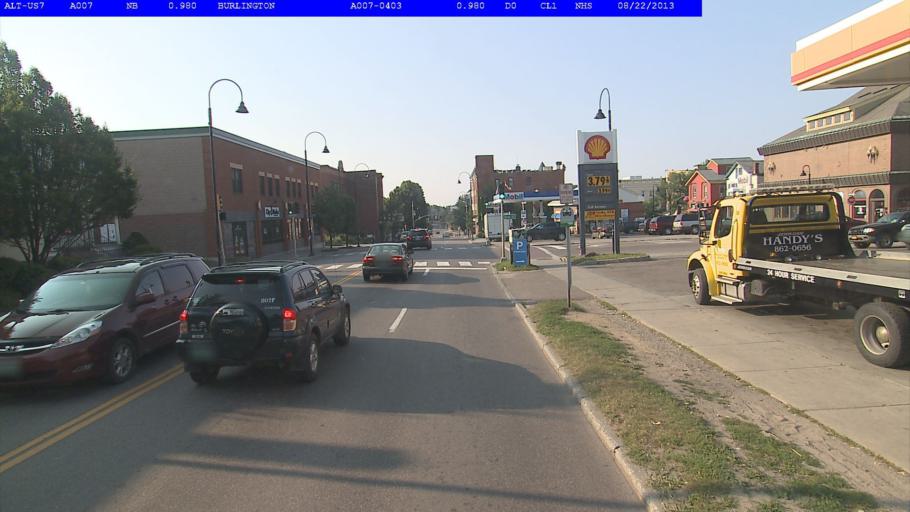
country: US
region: Vermont
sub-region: Chittenden County
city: Burlington
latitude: 44.4786
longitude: -73.2112
